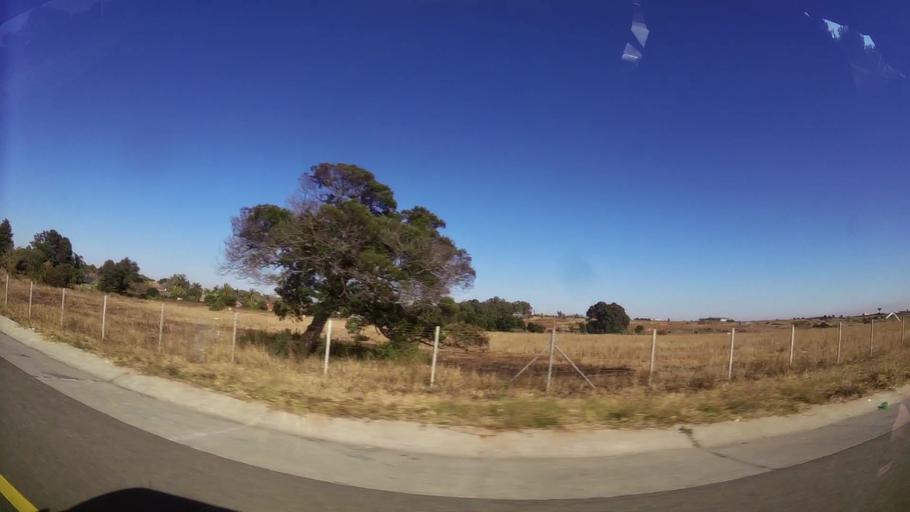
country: ZA
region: Gauteng
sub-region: City of Tshwane Metropolitan Municipality
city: Centurion
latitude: -25.8232
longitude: 28.2401
